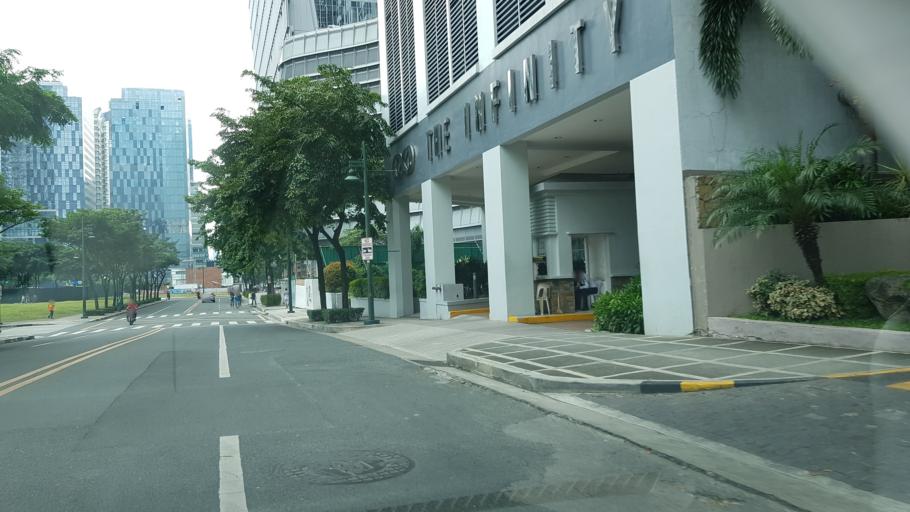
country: PH
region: Metro Manila
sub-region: Makati City
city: Makati City
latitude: 14.5467
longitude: 121.0516
